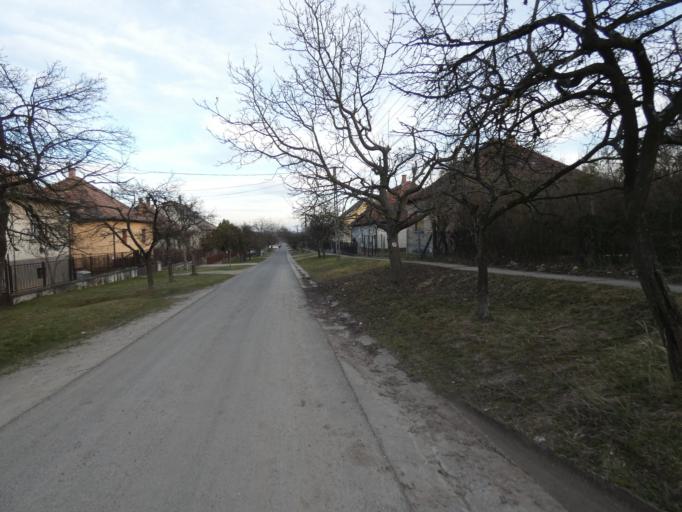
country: HU
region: Nograd
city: Diosjeno
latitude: 47.9442
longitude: 19.0342
